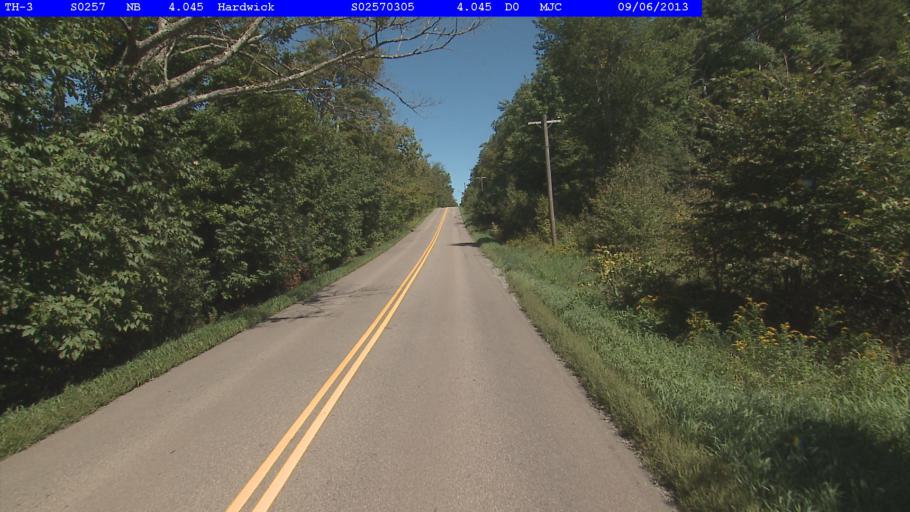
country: US
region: Vermont
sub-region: Caledonia County
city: Hardwick
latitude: 44.5463
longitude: -72.3233
